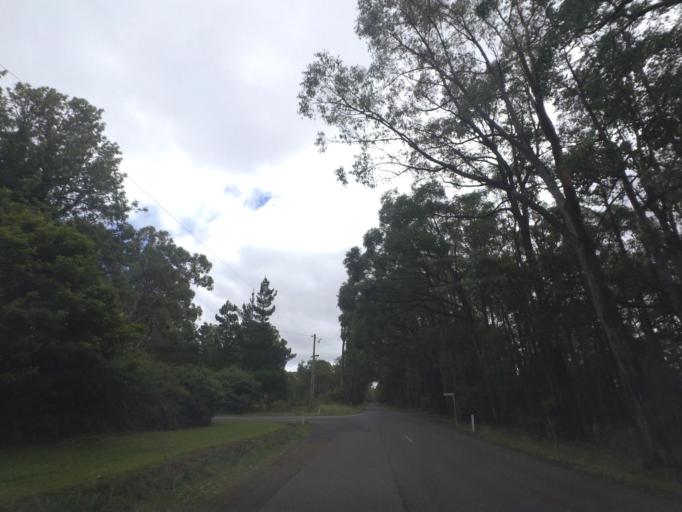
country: AU
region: Victoria
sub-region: Yarra Ranges
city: Launching Place
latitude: -37.8173
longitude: 145.5761
